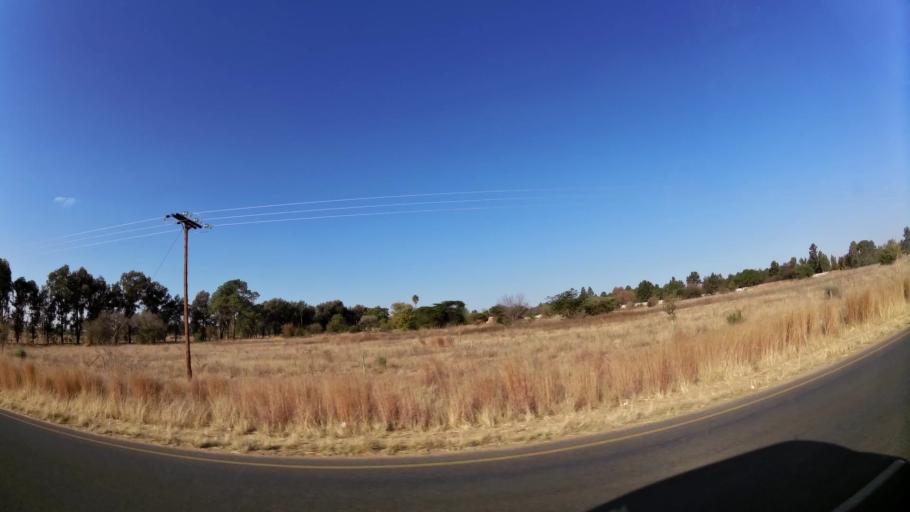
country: ZA
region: Gauteng
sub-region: West Rand District Municipality
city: Muldersdriseloop
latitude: -26.0165
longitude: 27.9094
